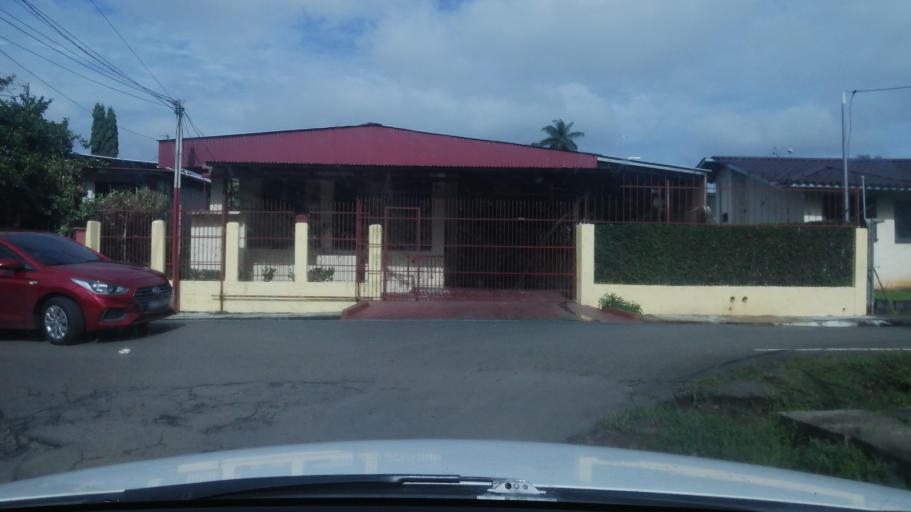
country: PA
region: Chiriqui
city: David
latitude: 8.4104
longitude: -82.4349
